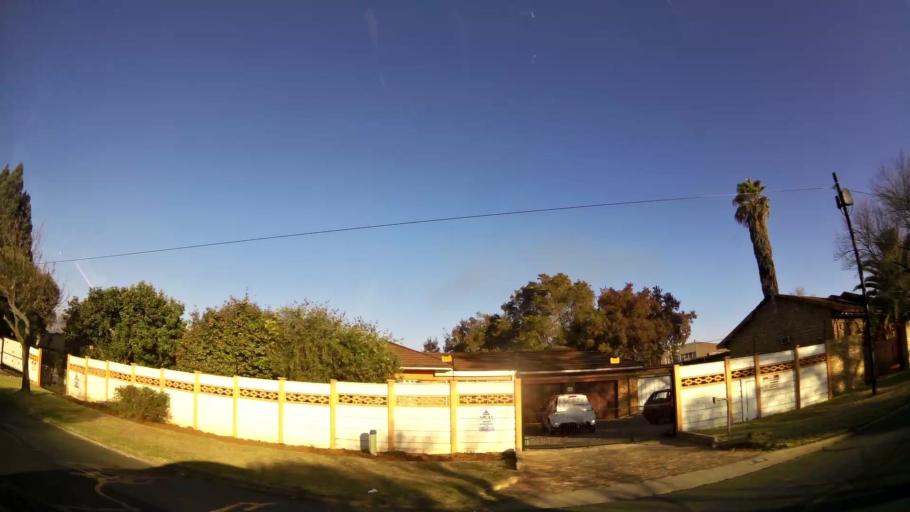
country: ZA
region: Gauteng
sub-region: City of Johannesburg Metropolitan Municipality
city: Roodepoort
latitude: -26.1839
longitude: 27.9236
